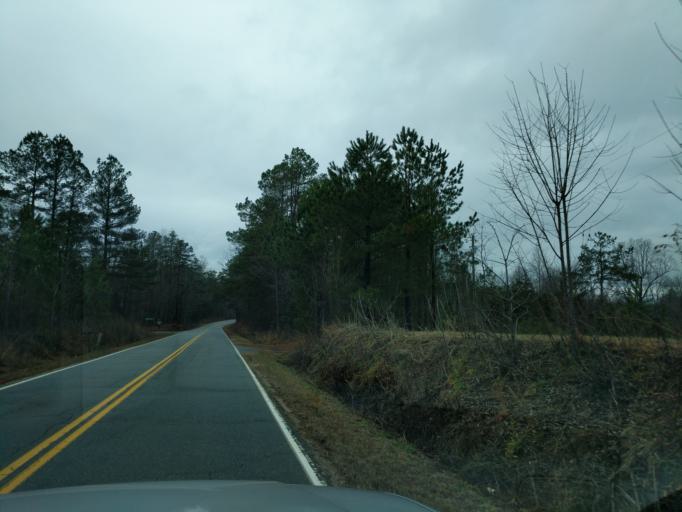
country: US
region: South Carolina
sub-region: Oconee County
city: Walhalla
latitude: 34.7983
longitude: -83.1608
